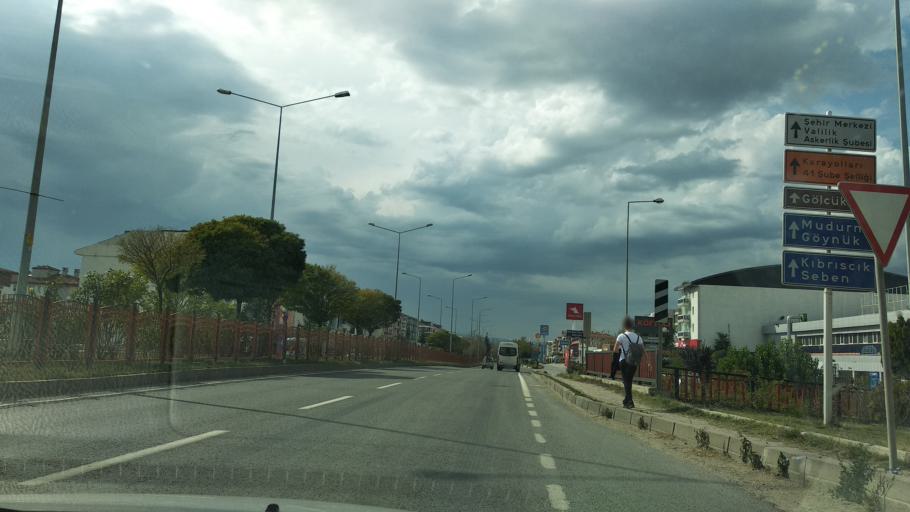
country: TR
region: Bolu
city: Bolu
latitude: 40.7377
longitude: 31.5996
